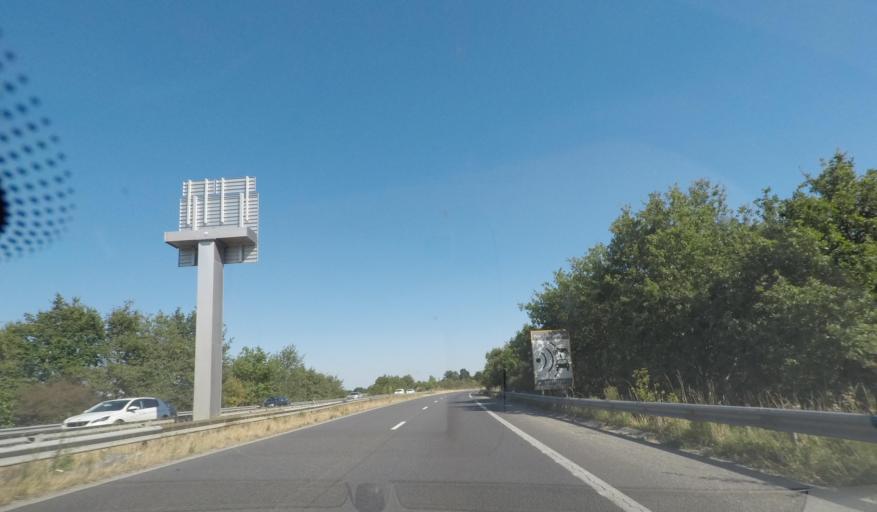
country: FR
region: Pays de la Loire
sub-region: Departement de la Loire-Atlantique
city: Pontchateau
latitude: 47.4457
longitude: -2.0868
